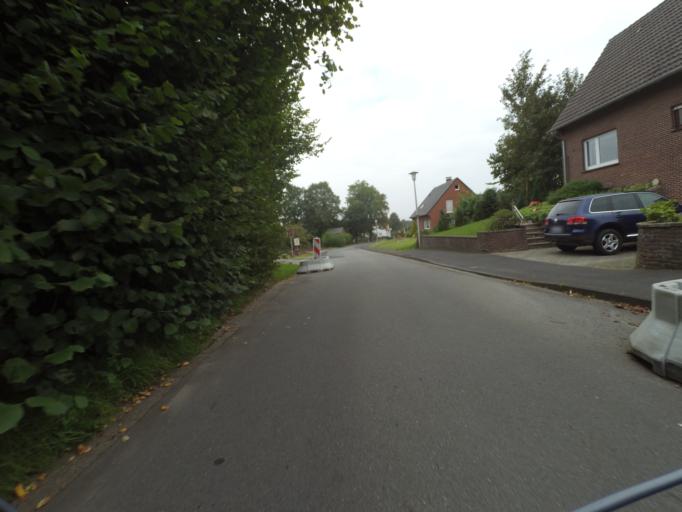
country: DE
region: Lower Saxony
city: Bad Bentheim
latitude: 52.2960
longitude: 7.0940
